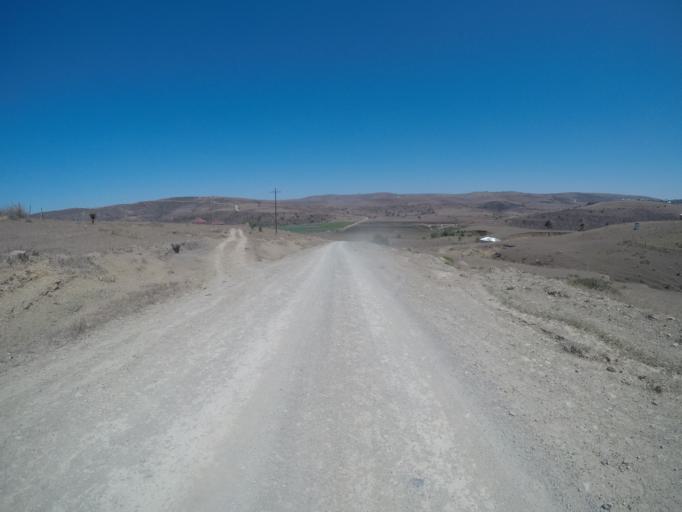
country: ZA
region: Eastern Cape
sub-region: OR Tambo District Municipality
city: Mthatha
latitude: -31.8649
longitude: 28.8724
